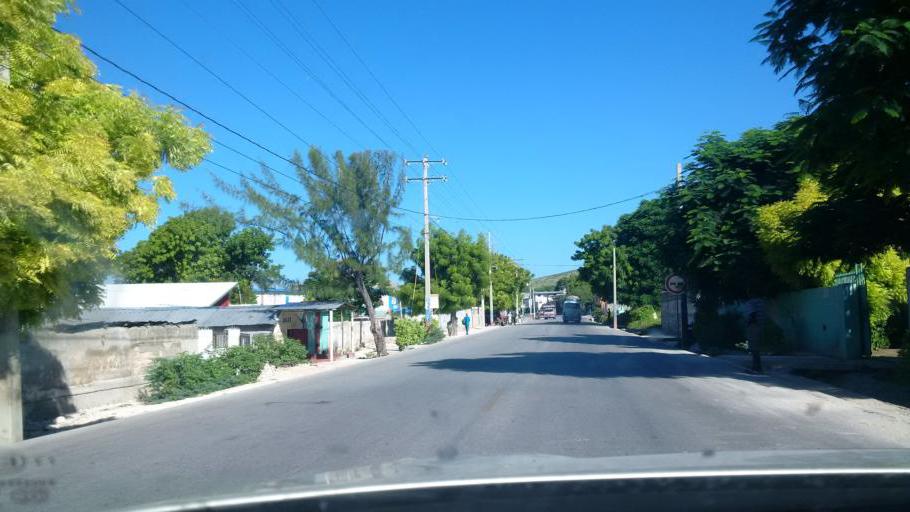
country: HT
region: Ouest
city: Cabaret
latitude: 18.7211
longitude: -72.3737
